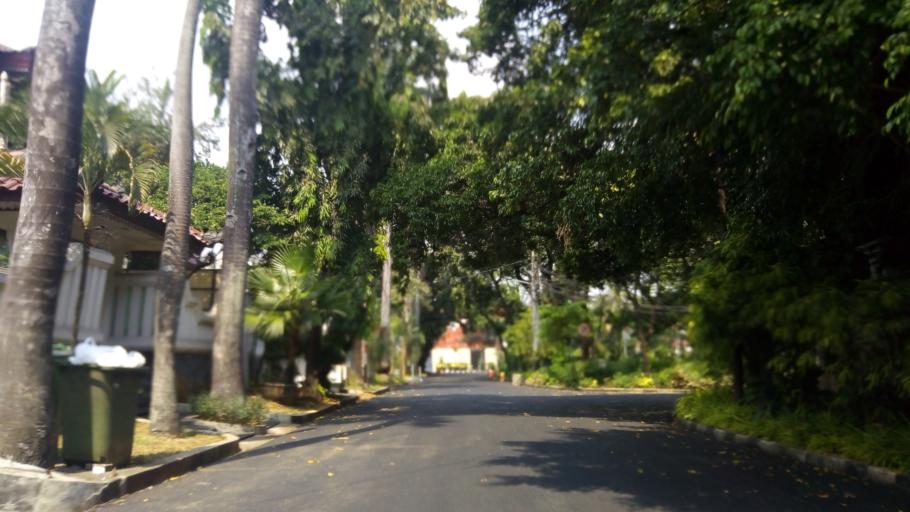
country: ID
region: Jakarta Raya
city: Jakarta
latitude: -6.1971
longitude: 106.8277
